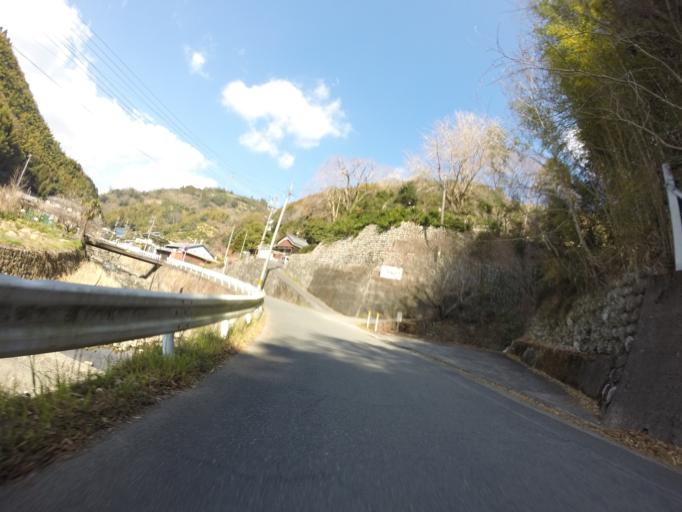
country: JP
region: Shizuoka
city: Shizuoka-shi
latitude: 35.0739
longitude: 138.4852
